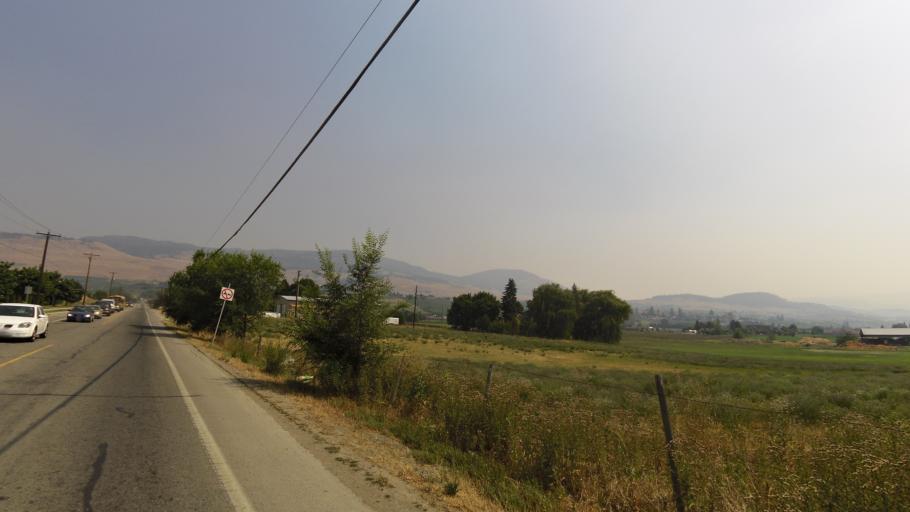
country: CA
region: British Columbia
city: Kelowna
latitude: 49.9181
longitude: -119.3819
